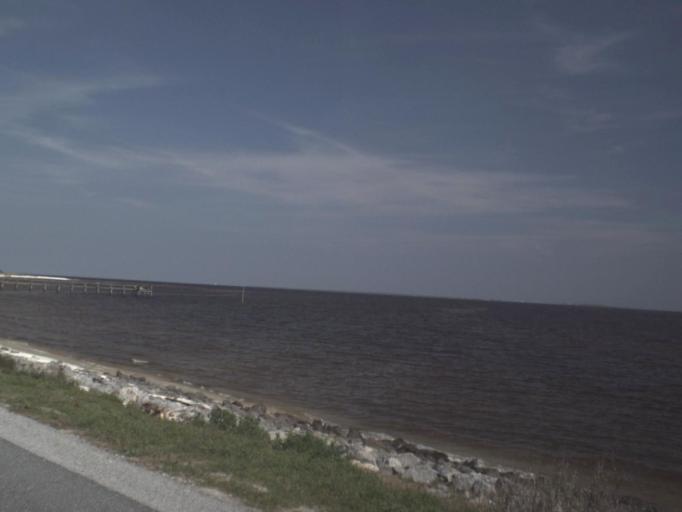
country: US
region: Florida
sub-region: Franklin County
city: Carrabelle
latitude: 29.8037
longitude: -84.7368
